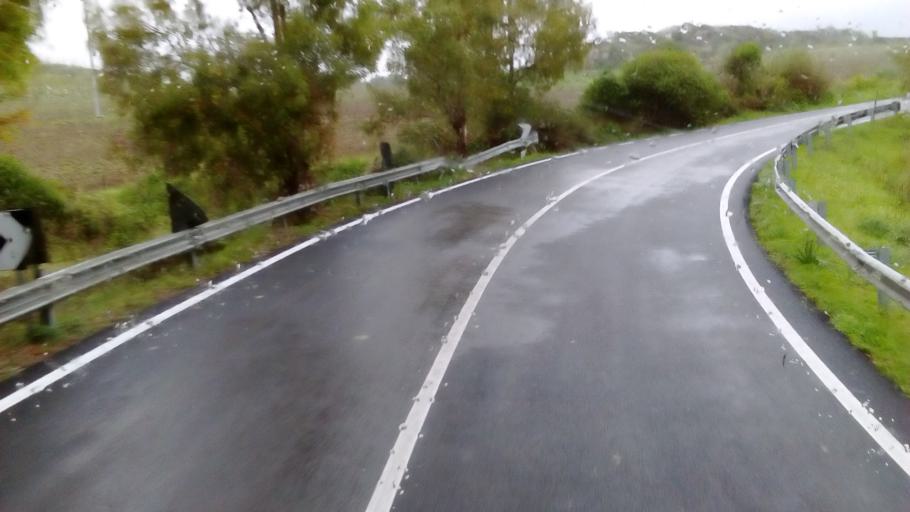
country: IT
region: Sicily
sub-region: Enna
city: Pietraperzia
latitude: 37.4611
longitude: 14.1770
